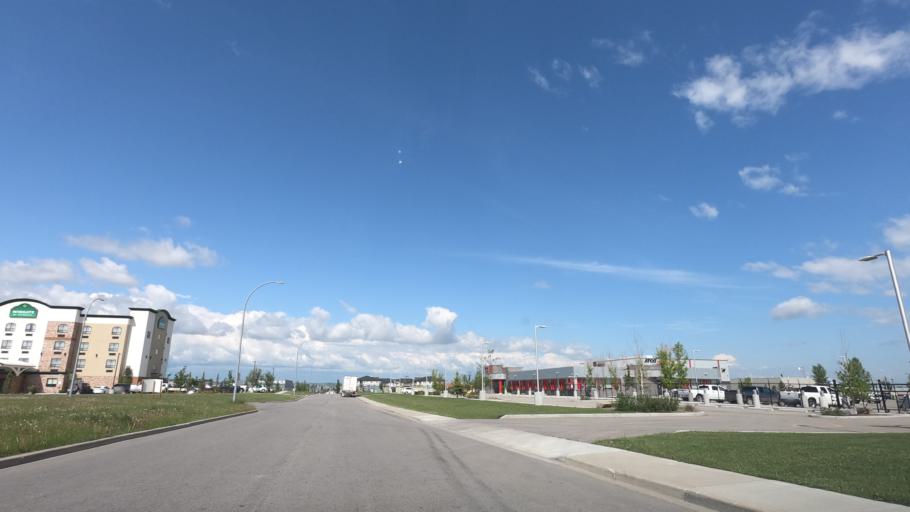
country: CA
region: Alberta
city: Airdrie
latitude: 51.3040
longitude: -114.0065
